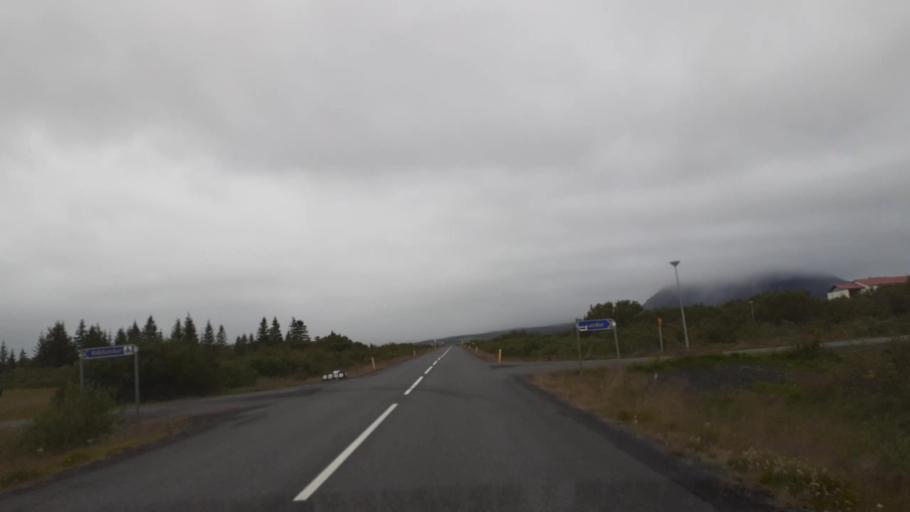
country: IS
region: Northeast
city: Husavik
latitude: 66.0738
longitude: -16.4348
